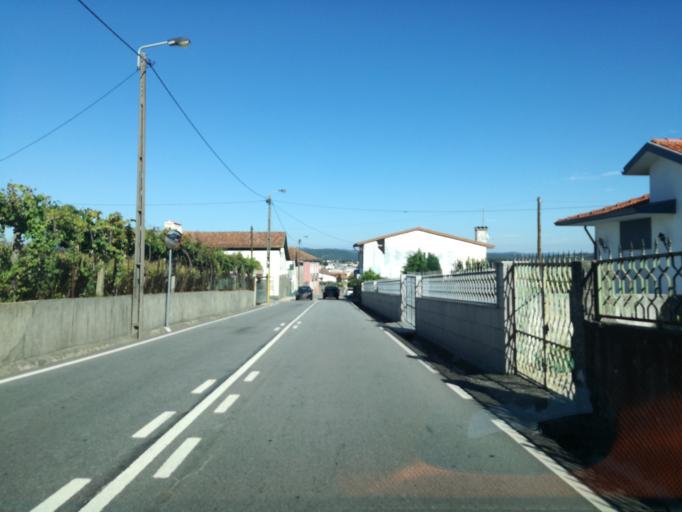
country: PT
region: Porto
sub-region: Trofa
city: Sao Romao do Coronado
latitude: 41.2841
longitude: -8.5781
